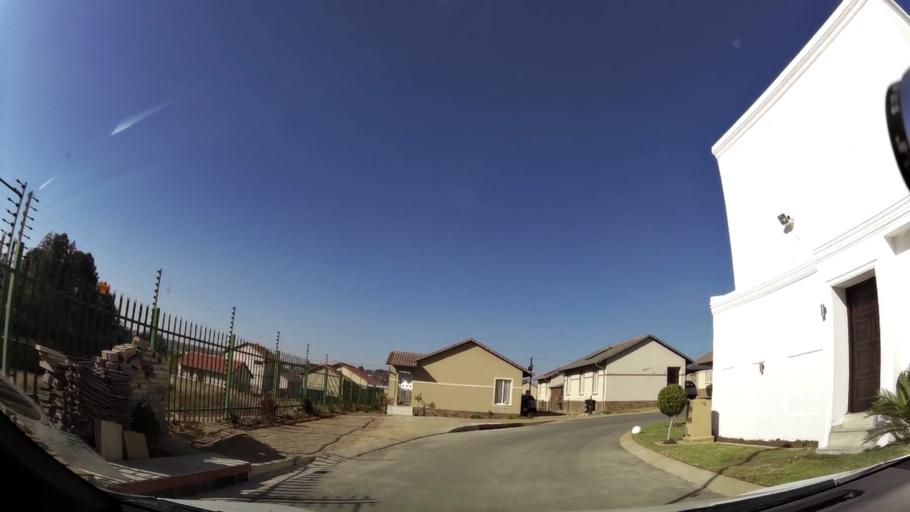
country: ZA
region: Gauteng
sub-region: City of Johannesburg Metropolitan Municipality
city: Diepsloot
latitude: -26.0177
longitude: 27.9657
